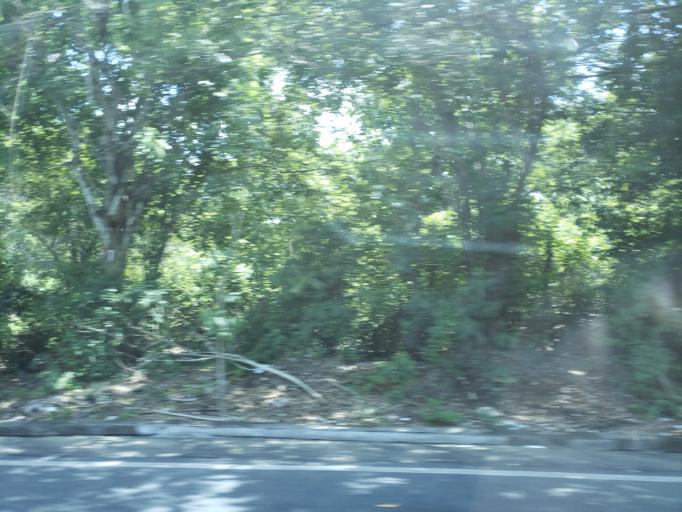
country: ID
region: Bali
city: Jimbaran
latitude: -8.7879
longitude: 115.1650
